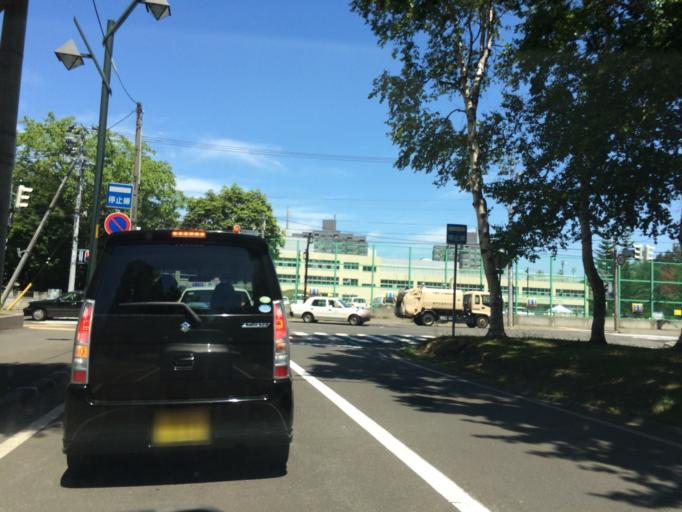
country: JP
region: Hokkaido
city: Sapporo
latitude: 42.9889
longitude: 141.3545
